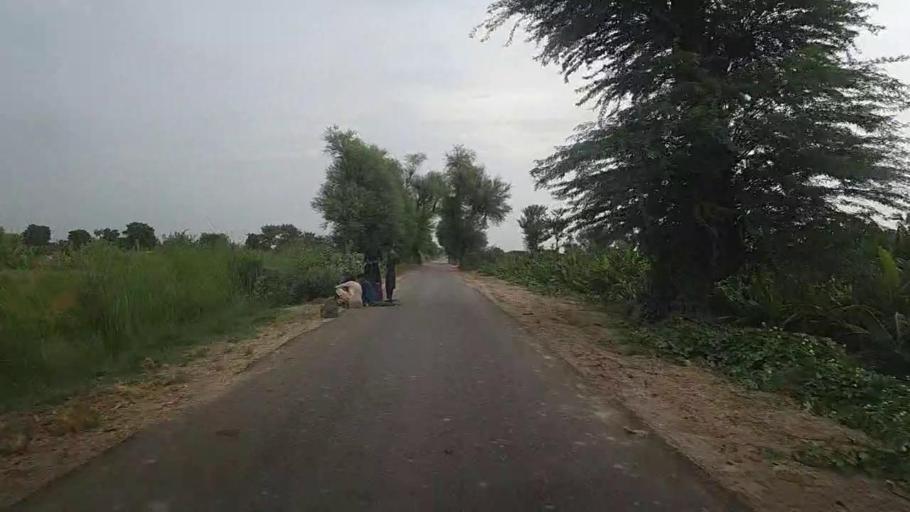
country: PK
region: Sindh
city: Karaundi
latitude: 26.9747
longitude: 68.3599
